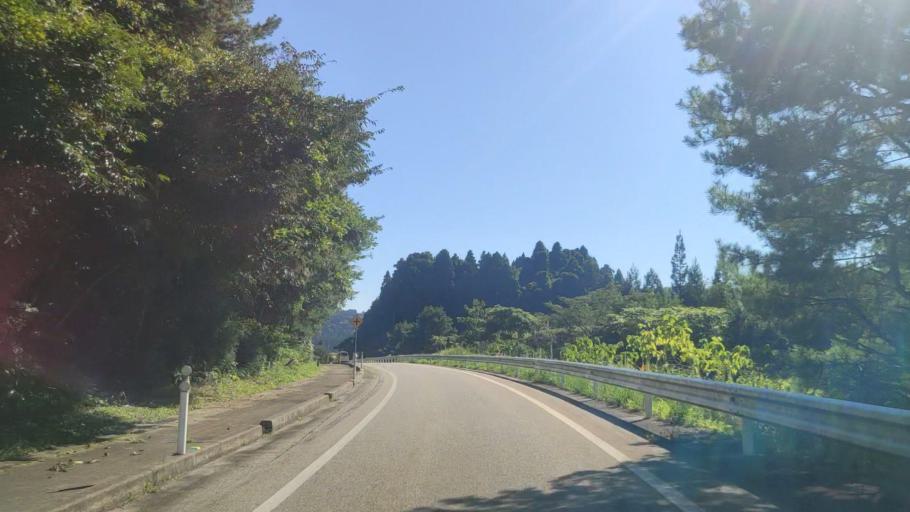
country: JP
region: Ishikawa
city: Nanao
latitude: 37.3945
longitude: 137.2342
